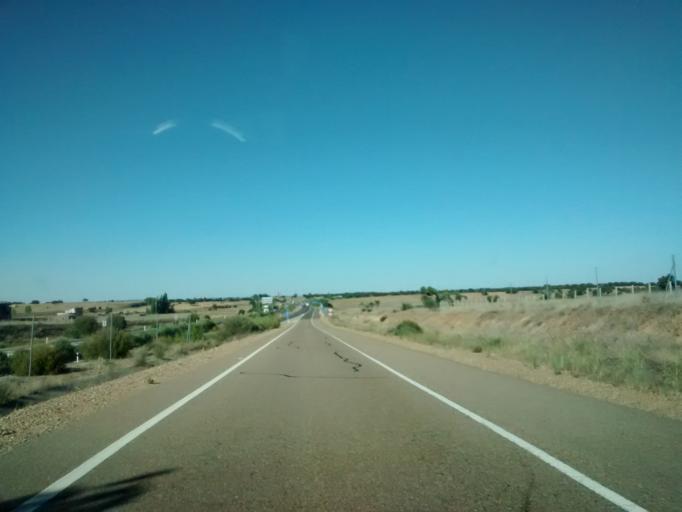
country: ES
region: Castille and Leon
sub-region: Provincia de Salamanca
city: Martin de Yeltes
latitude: 40.7716
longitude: -6.2840
